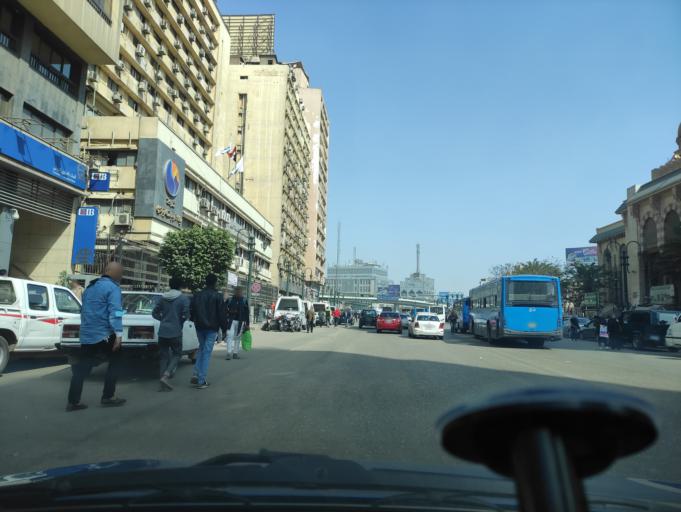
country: EG
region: Muhafazat al Qahirah
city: Cairo
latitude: 30.0597
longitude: 31.2451
